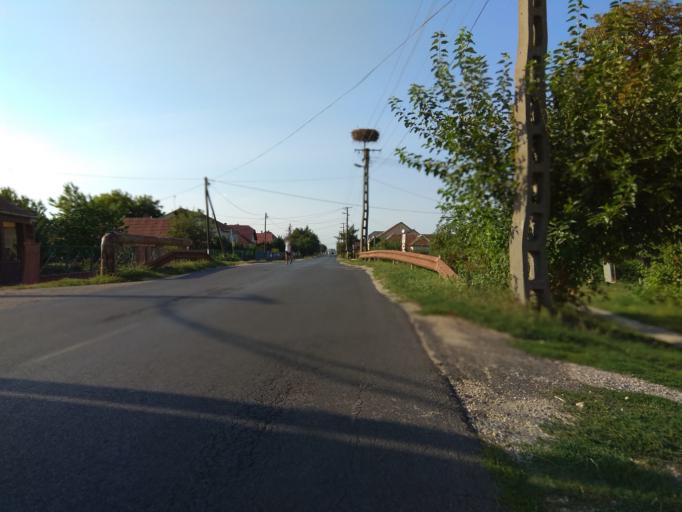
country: HU
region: Borsod-Abauj-Zemplen
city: Onod
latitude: 48.0085
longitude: 20.9121
